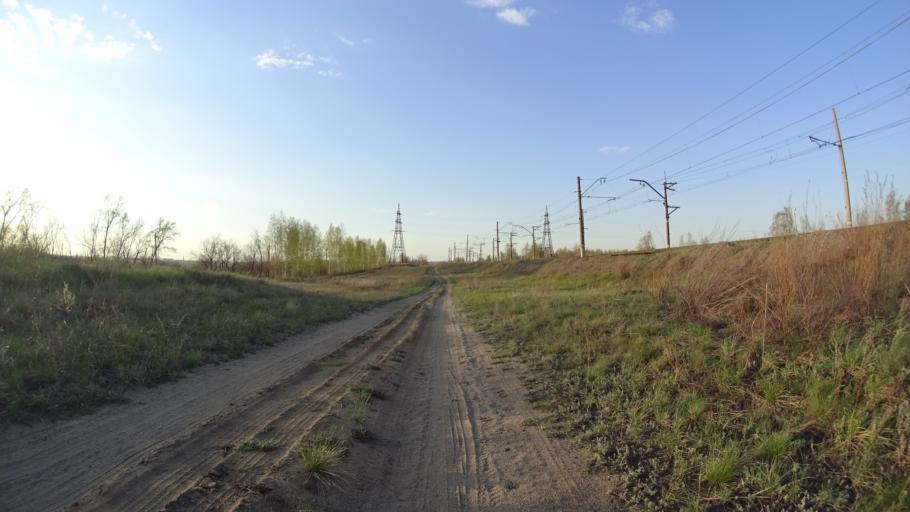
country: RU
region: Chelyabinsk
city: Troitsk
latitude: 54.0594
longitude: 61.6136
